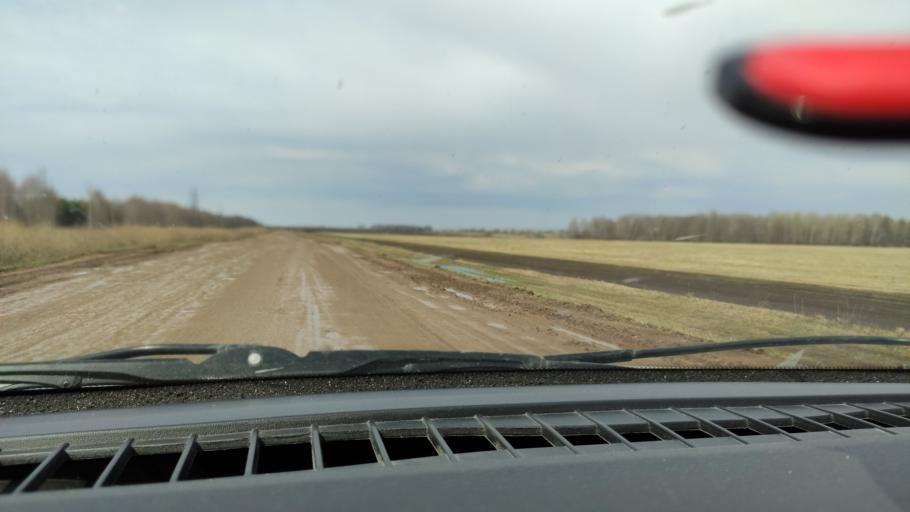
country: RU
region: Bashkortostan
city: Burayevo
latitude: 55.6552
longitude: 55.1717
